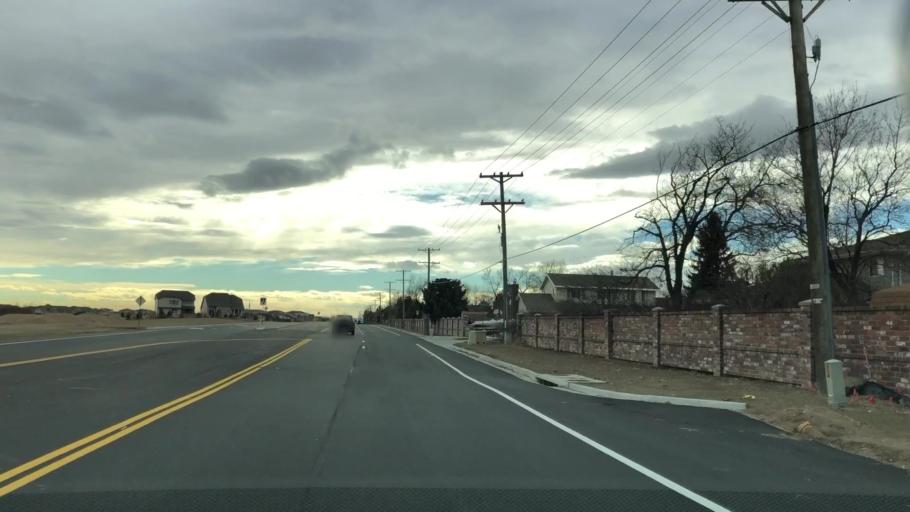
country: US
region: Colorado
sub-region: Larimer County
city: Loveland
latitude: 40.4274
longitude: -105.0209
